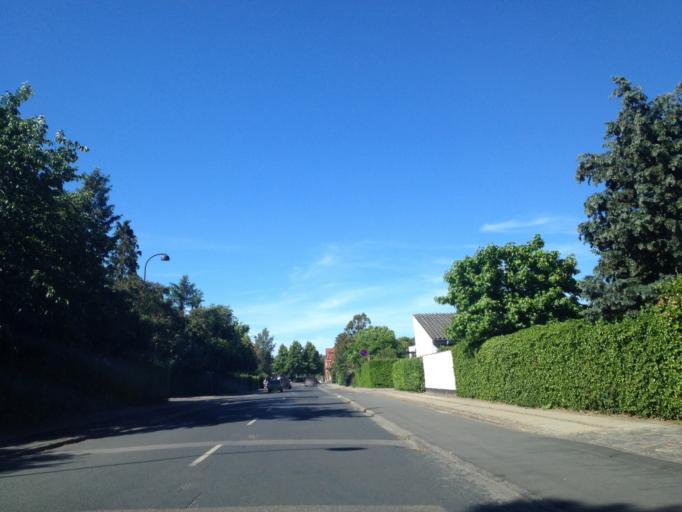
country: DK
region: Capital Region
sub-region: Gentofte Kommune
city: Charlottenlund
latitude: 55.7583
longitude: 12.5853
